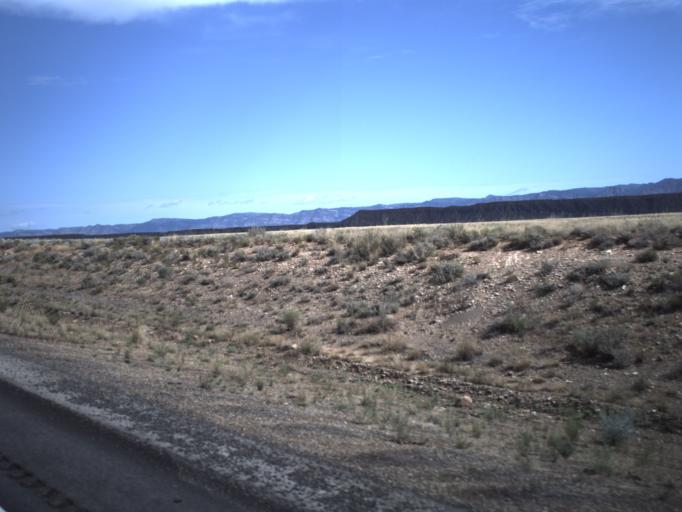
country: US
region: Utah
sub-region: Carbon County
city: East Carbon City
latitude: 39.4783
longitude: -110.5074
